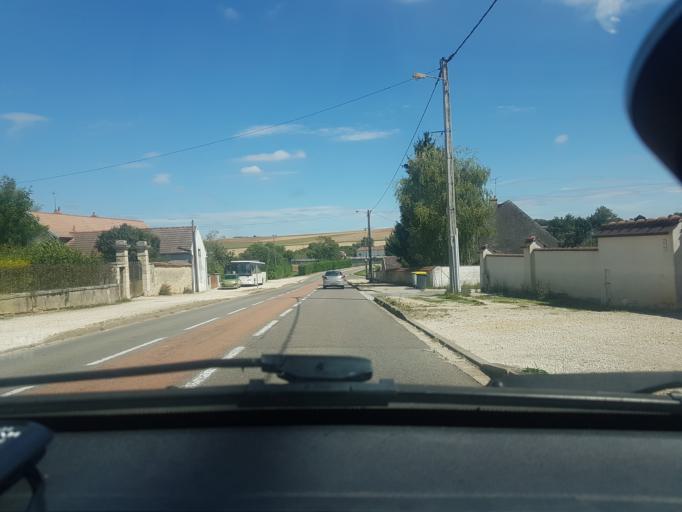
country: FR
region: Bourgogne
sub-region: Departement de la Cote-d'Or
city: Belleneuve
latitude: 47.3811
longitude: 5.2557
